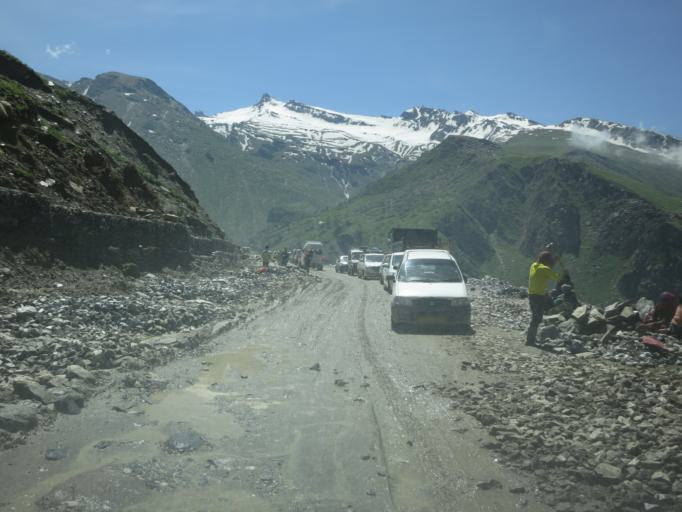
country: IN
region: Himachal Pradesh
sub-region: Kulu
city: Manali
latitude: 32.3542
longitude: 77.2158
